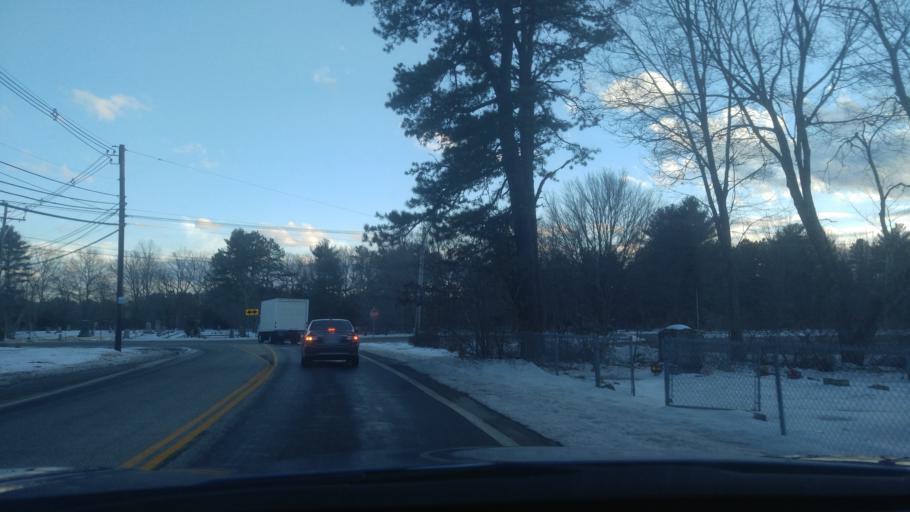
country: US
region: Rhode Island
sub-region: Kent County
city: West Greenwich
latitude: 41.6695
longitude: -71.6049
